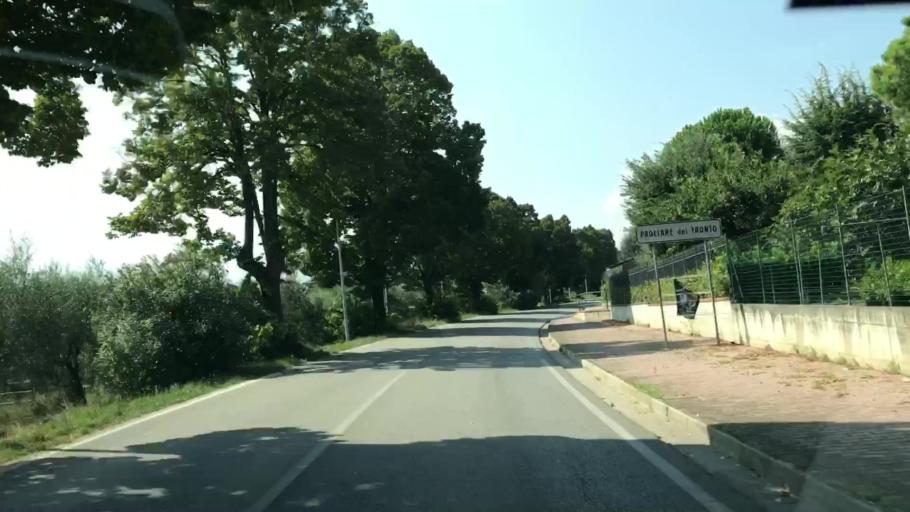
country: IT
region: The Marches
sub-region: Provincia di Ascoli Piceno
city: Pagliare
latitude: 42.8748
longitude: 13.7728
